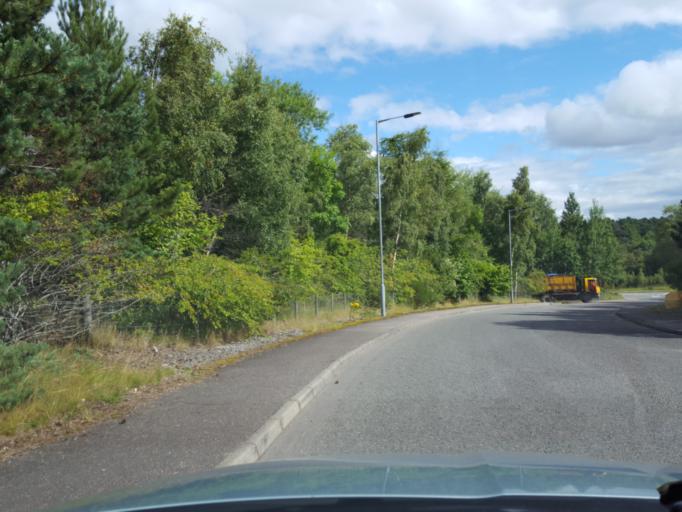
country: GB
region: Scotland
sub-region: Highland
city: Grantown on Spey
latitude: 57.3185
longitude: -3.6068
